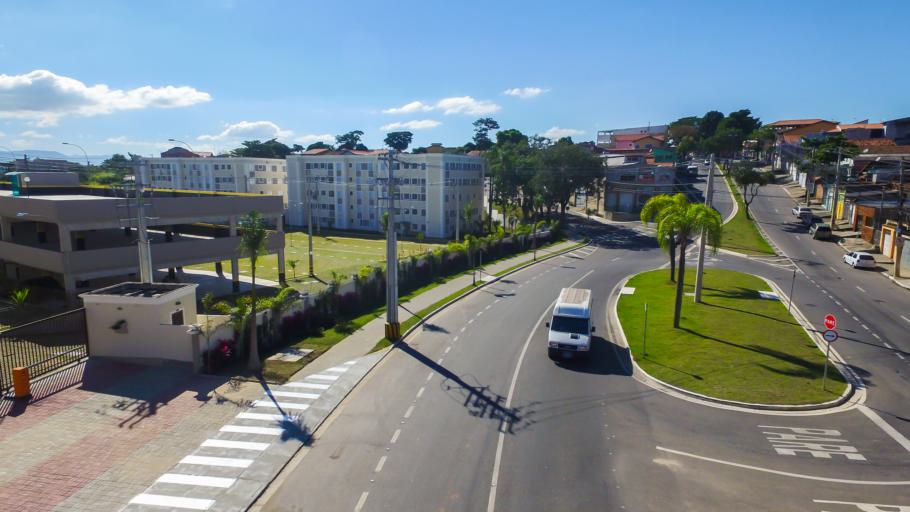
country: BR
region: Sao Paulo
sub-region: Sao Jose Dos Campos
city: Sao Jose dos Campos
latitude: -23.1721
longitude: -45.8450
